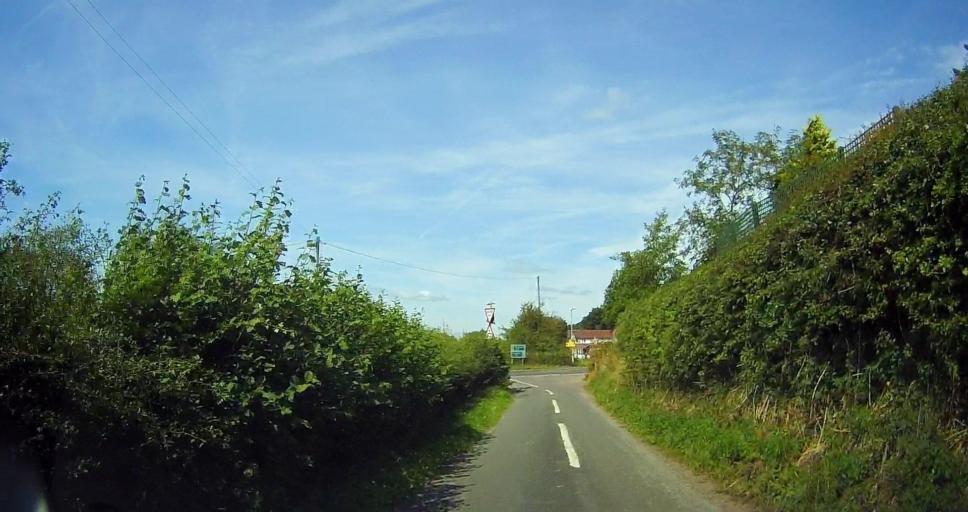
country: GB
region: England
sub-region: Shropshire
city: Market Drayton
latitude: 52.9831
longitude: -2.5181
